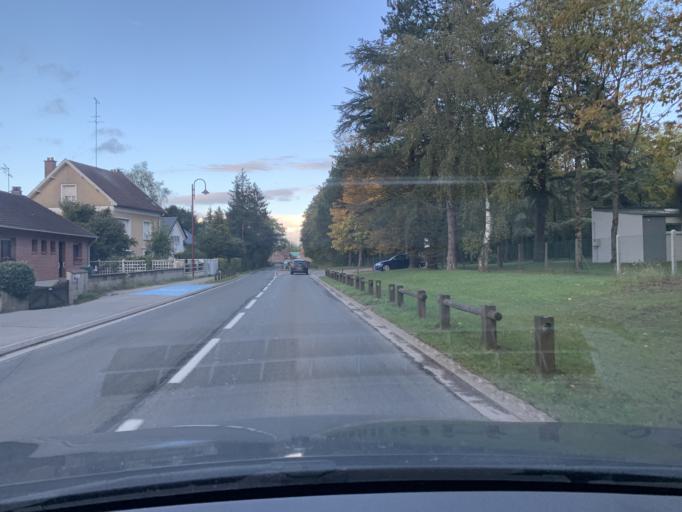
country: FR
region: Nord-Pas-de-Calais
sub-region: Departement du Nord
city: Proville
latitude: 50.1606
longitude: 3.2121
